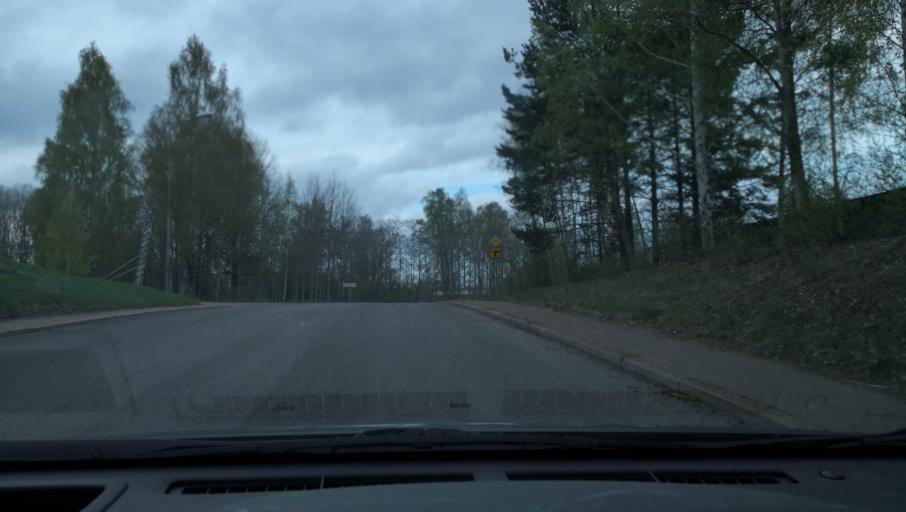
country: SE
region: Dalarna
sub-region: Avesta Kommun
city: Avesta
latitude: 60.1215
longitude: 16.2103
